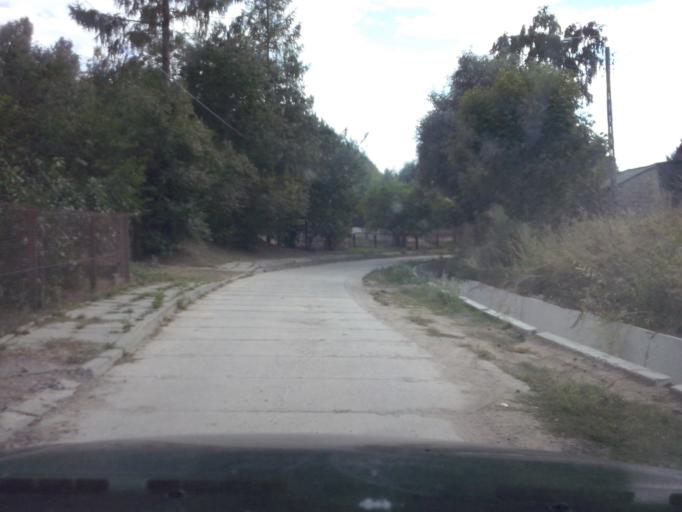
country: PL
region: Swietokrzyskie
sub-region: Powiat kielecki
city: Lagow
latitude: 50.7816
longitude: 21.0895
